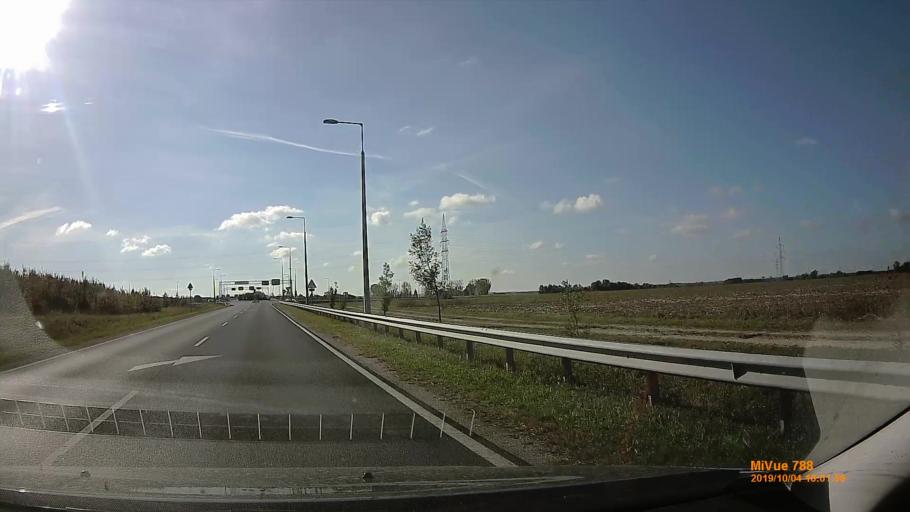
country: HU
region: Somogy
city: Kaposvar
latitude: 46.4005
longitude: 17.7754
